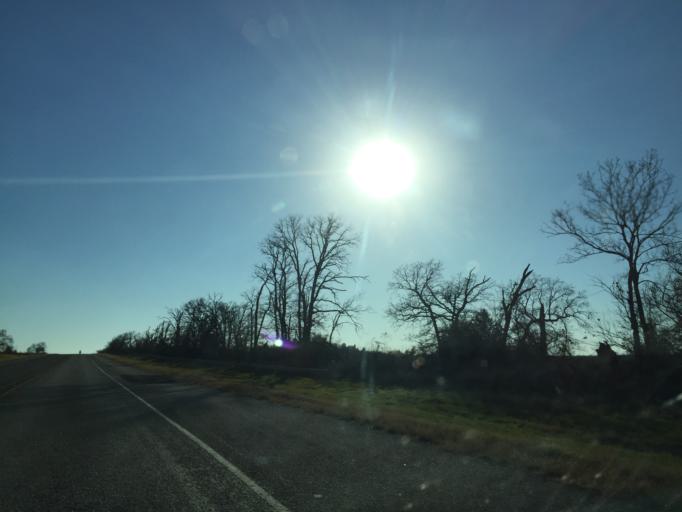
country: US
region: Texas
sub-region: Bastrop County
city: Elgin
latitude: 30.3665
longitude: -97.2642
